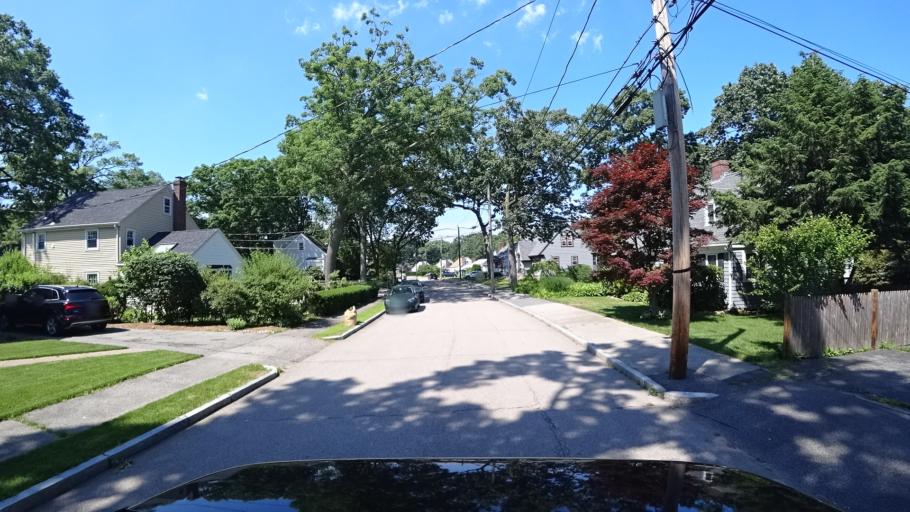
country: US
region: Massachusetts
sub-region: Norfolk County
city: Dedham
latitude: 42.2689
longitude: -71.1682
